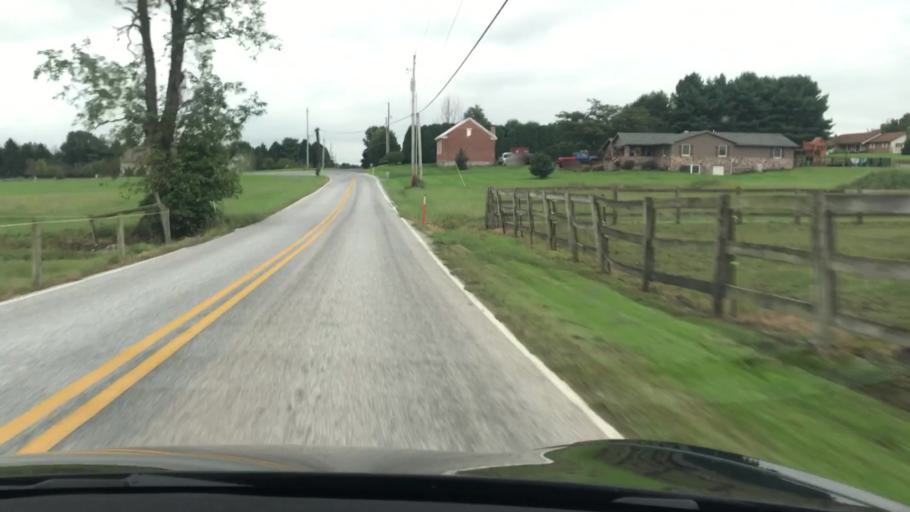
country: US
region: Pennsylvania
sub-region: York County
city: Dillsburg
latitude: 40.0620
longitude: -77.0848
